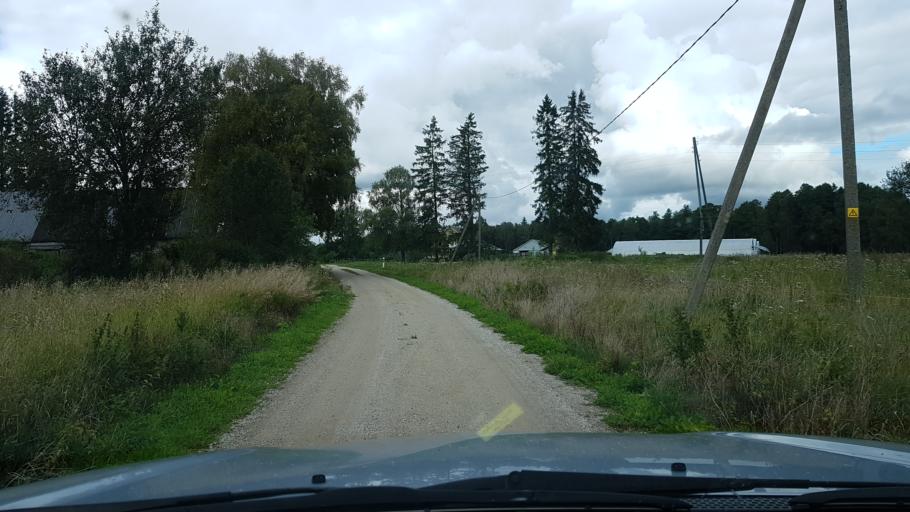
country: EE
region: Harju
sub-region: Raasiku vald
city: Arukula
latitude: 59.2753
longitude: 25.0951
